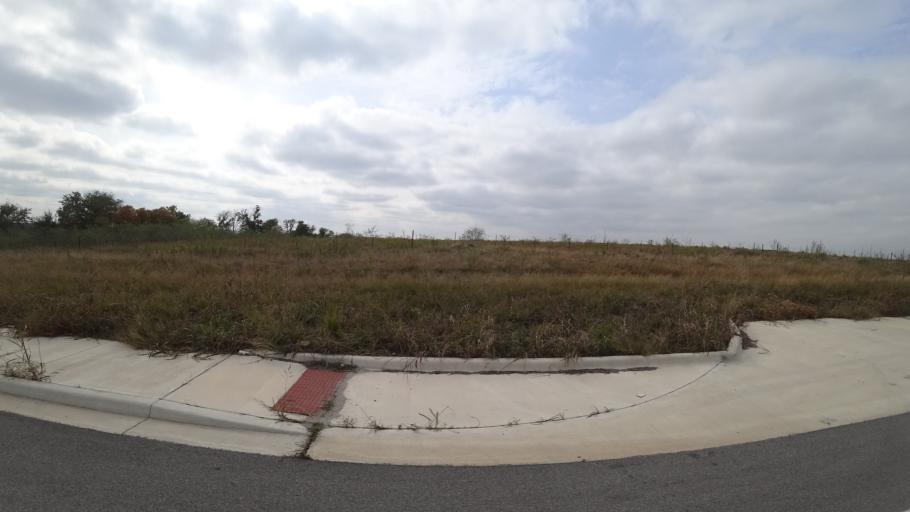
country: US
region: Texas
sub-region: Travis County
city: Manor
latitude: 30.3732
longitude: -97.5939
